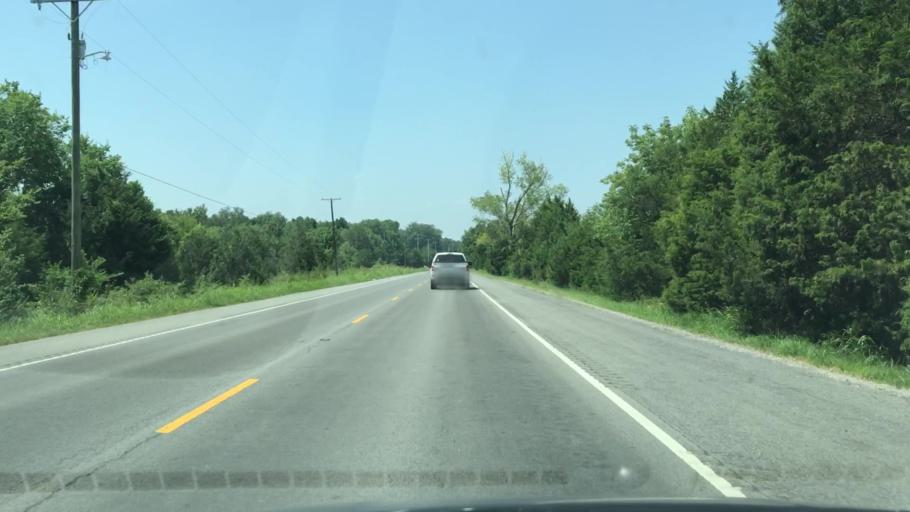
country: US
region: Tennessee
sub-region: Rutherford County
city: La Vergne
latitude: 36.0791
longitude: -86.5693
